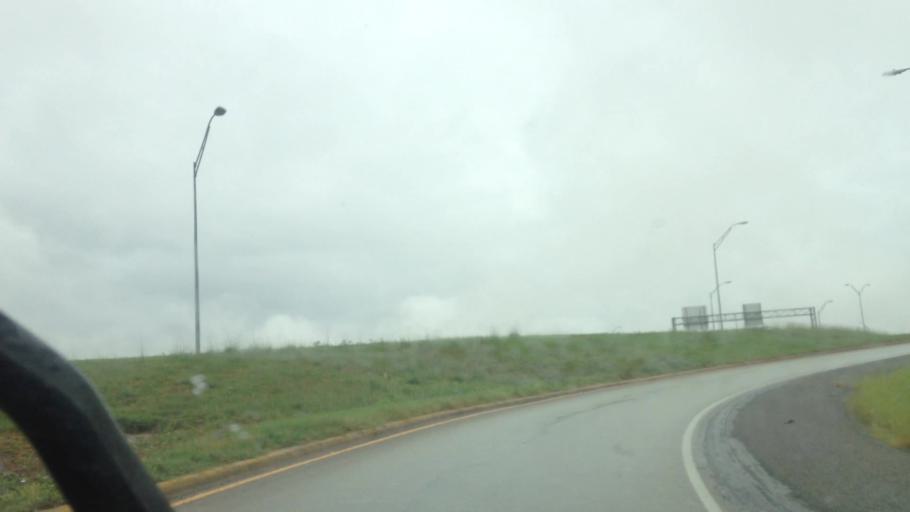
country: US
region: Texas
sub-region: Tarrant County
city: Saginaw
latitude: 32.8385
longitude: -97.3620
